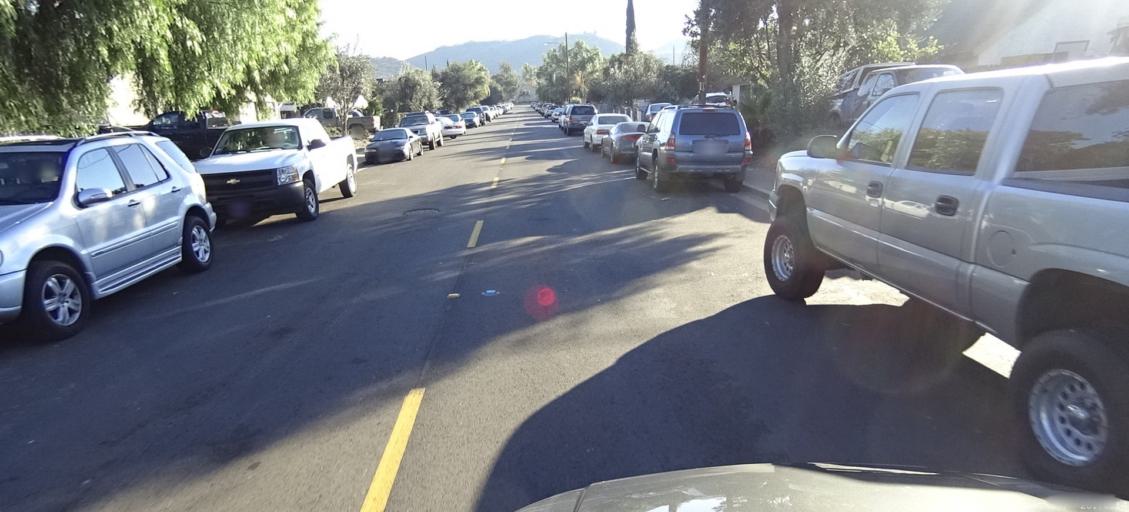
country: US
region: California
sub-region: Orange County
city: Villa Park
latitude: 33.7904
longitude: -117.8048
